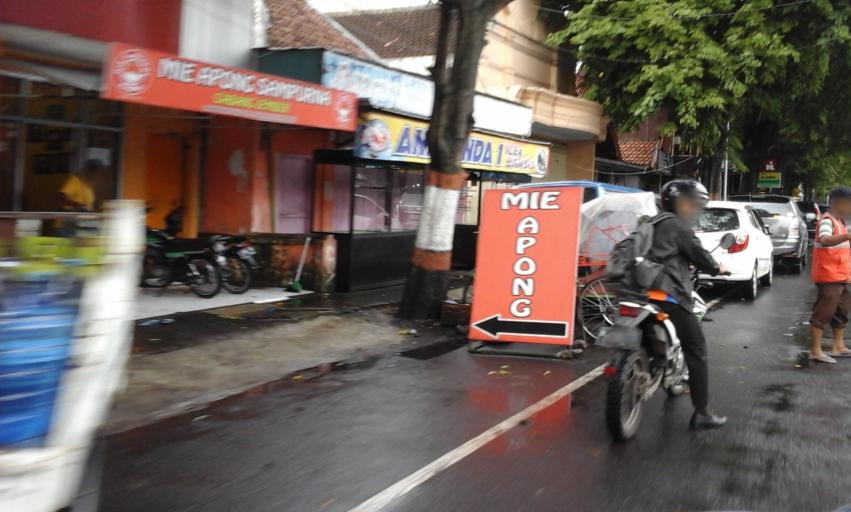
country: ID
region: East Java
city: Kadipaten
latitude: -8.1324
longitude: 113.2188
